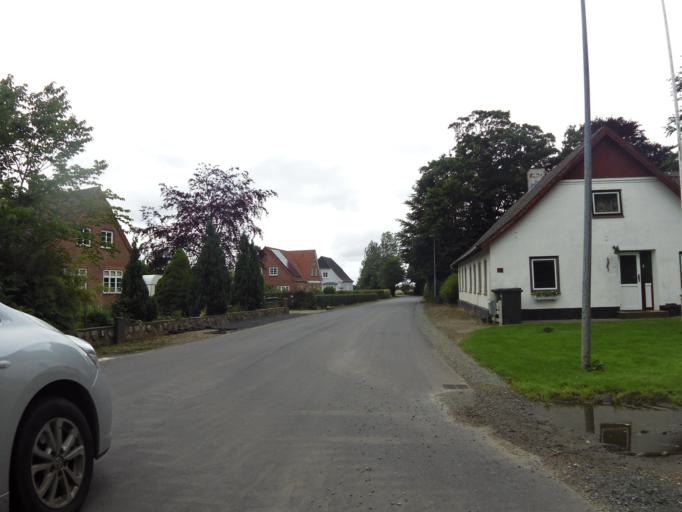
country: DK
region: South Denmark
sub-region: Tonder Kommune
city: Toftlund
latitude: 55.2544
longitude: 9.1582
